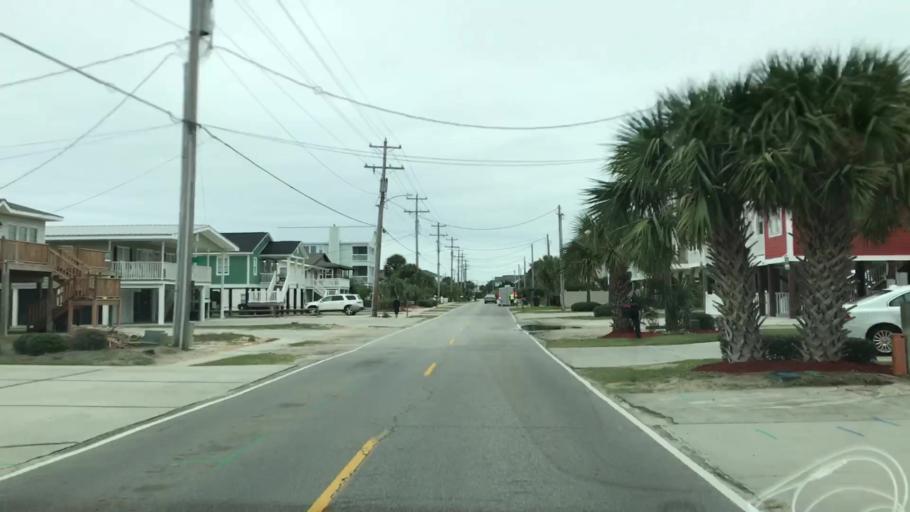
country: US
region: South Carolina
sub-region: Horry County
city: Garden City
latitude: 33.5638
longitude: -79.0101
